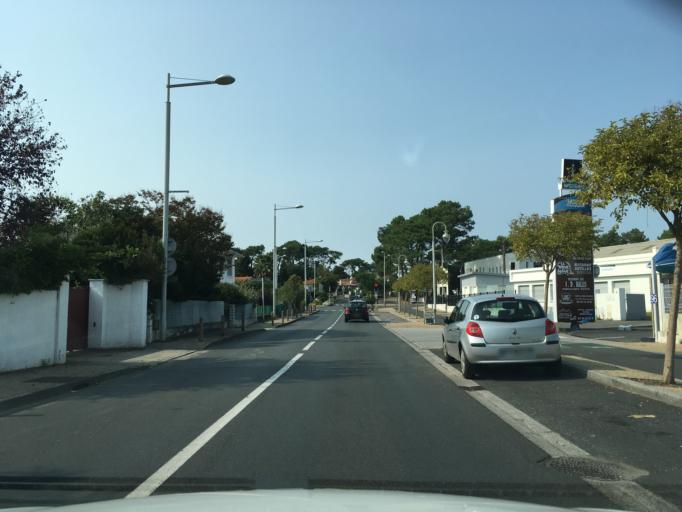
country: FR
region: Aquitaine
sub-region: Departement des Pyrenees-Atlantiques
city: Boucau
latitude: 43.5203
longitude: -1.5024
